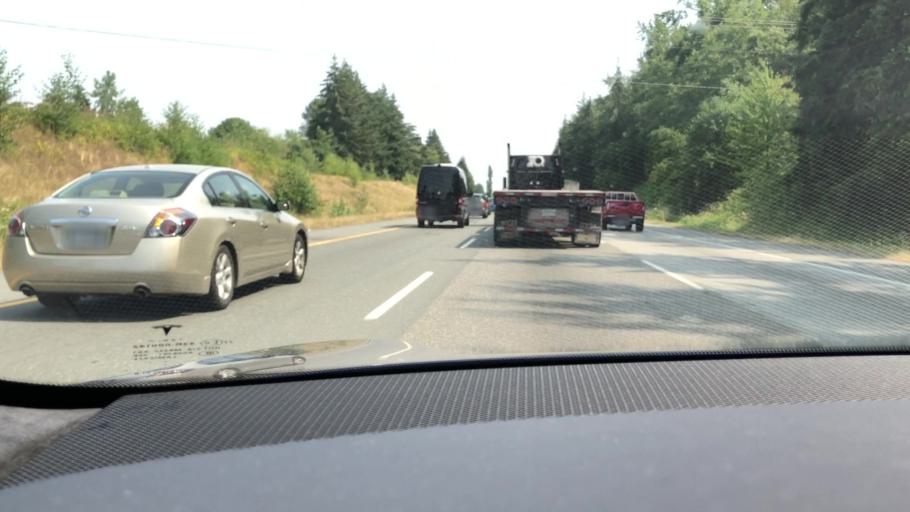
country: CA
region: British Columbia
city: Aldergrove
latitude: 49.1103
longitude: -122.5155
